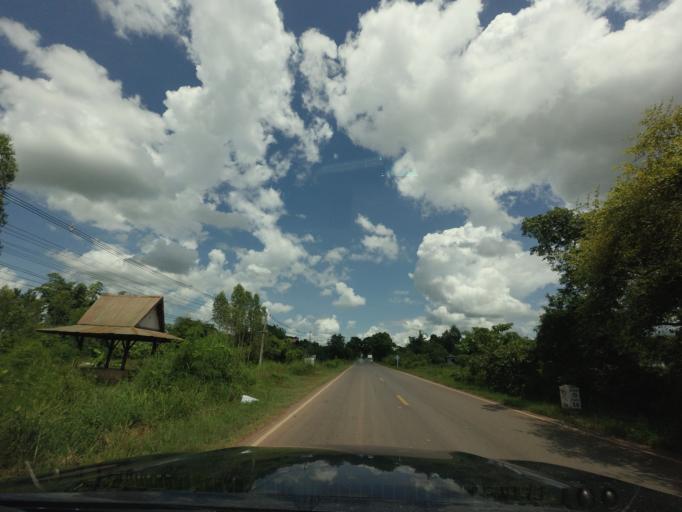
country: TH
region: Changwat Udon Thani
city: Ban Dung
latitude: 17.6753
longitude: 103.1782
